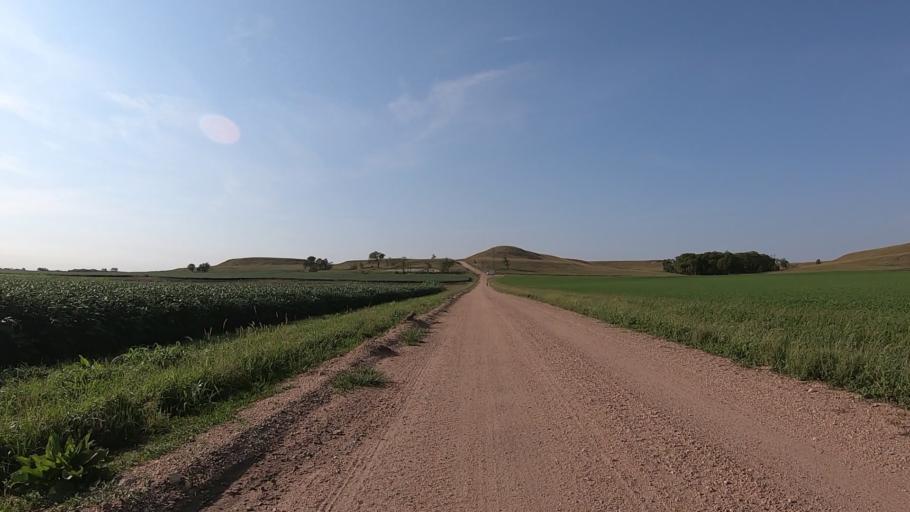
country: US
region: Kansas
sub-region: Marshall County
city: Blue Rapids
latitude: 39.6533
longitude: -96.8815
